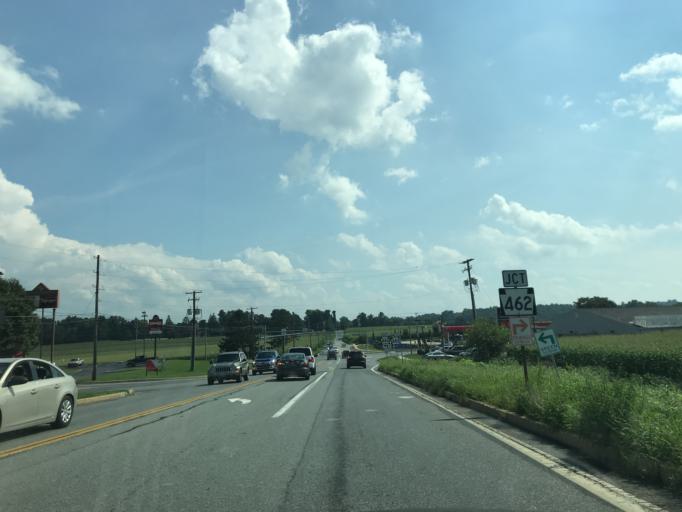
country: US
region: Pennsylvania
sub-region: Lancaster County
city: Mountville
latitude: 40.0378
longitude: -76.4553
